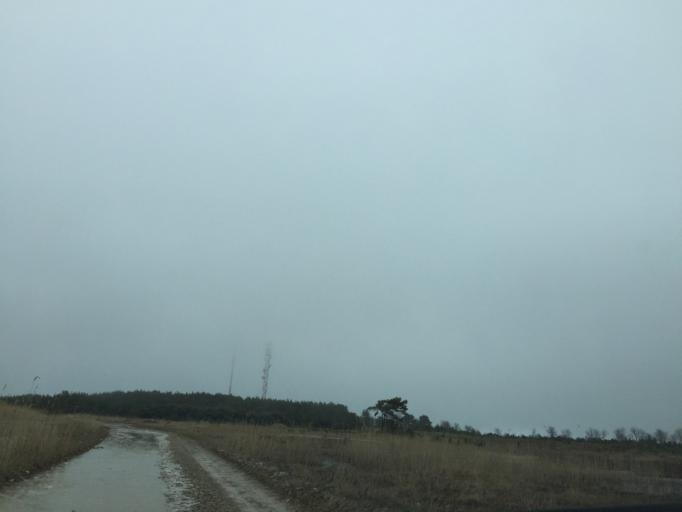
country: EE
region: Saare
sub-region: Kuressaare linn
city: Kuressaare
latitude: 58.5111
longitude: 21.9168
